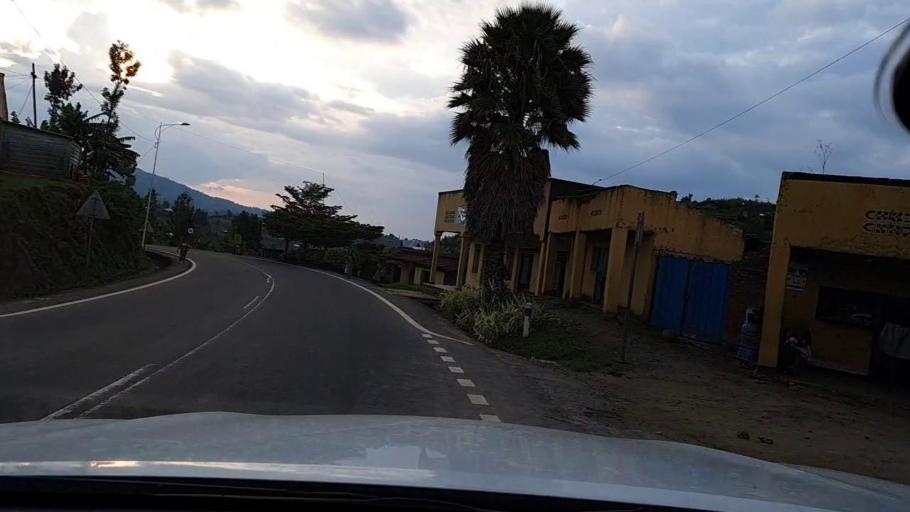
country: RW
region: Western Province
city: Kibuye
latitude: -2.0884
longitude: 29.4021
